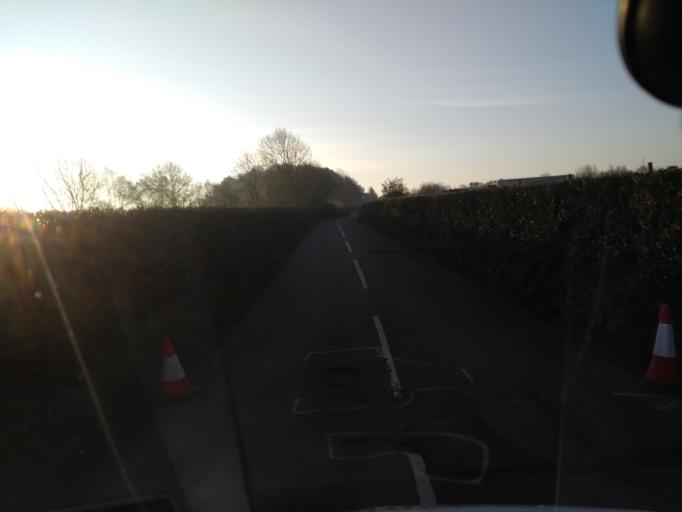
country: GB
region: England
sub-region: Somerset
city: Crewkerne
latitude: 50.8412
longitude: -2.8772
